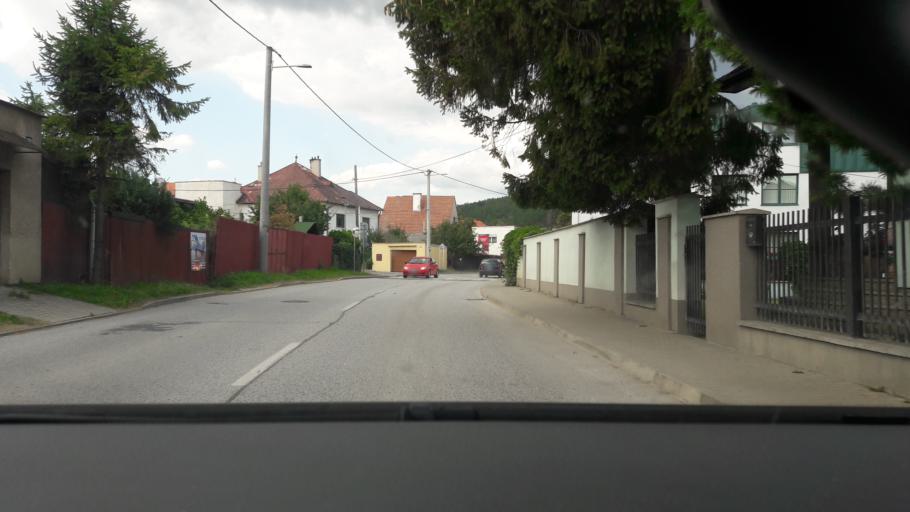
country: SK
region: Presovsky
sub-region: Okres Presov
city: Kezmarok
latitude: 49.1365
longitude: 20.4331
